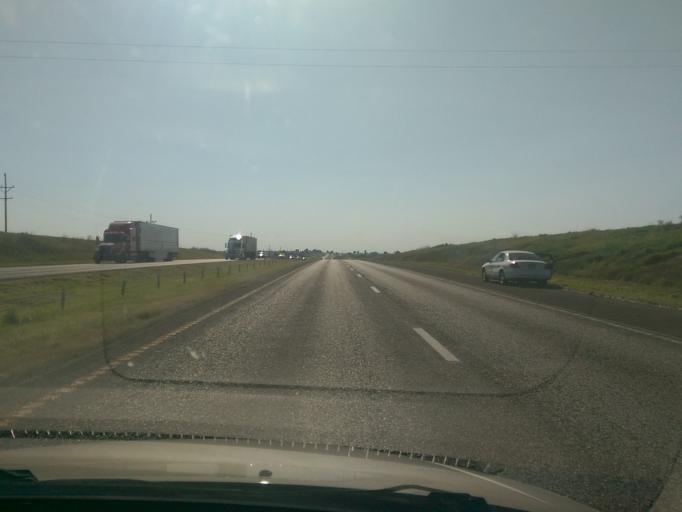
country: US
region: Missouri
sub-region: Lafayette County
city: Concordia
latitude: 38.9878
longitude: -93.5175
